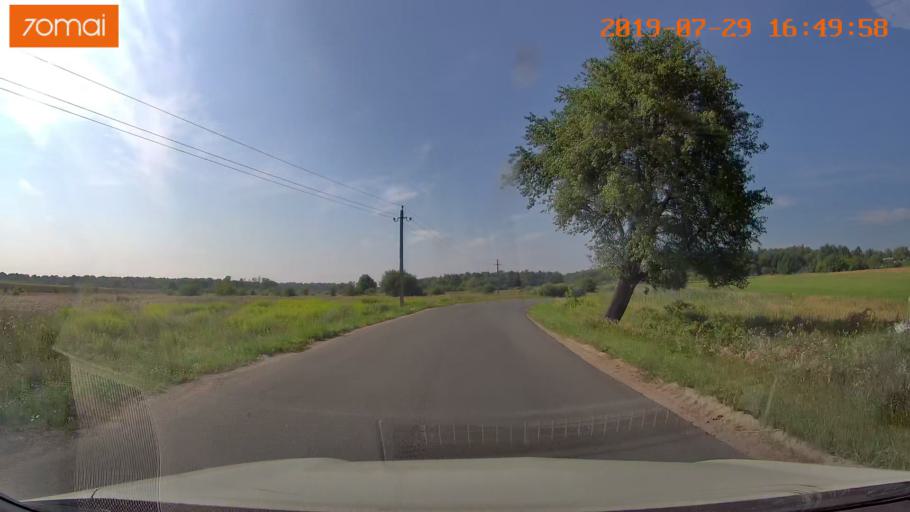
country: RU
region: Kaliningrad
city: Primorsk
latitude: 54.7988
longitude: 20.0591
